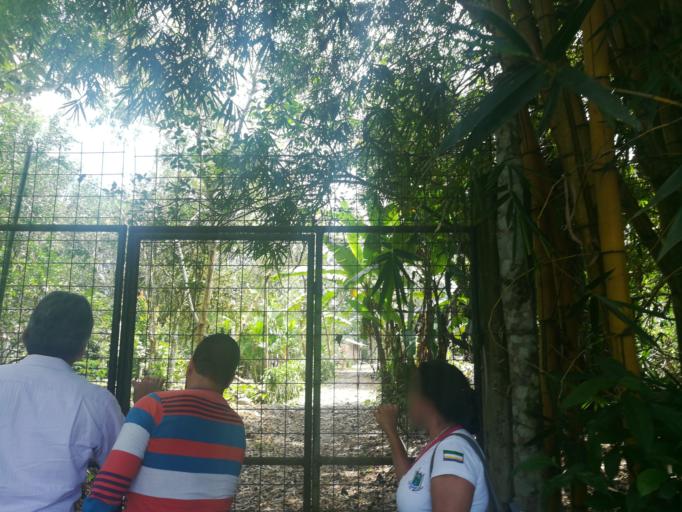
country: EC
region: Napo
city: Tena
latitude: -1.0297
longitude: -77.6774
